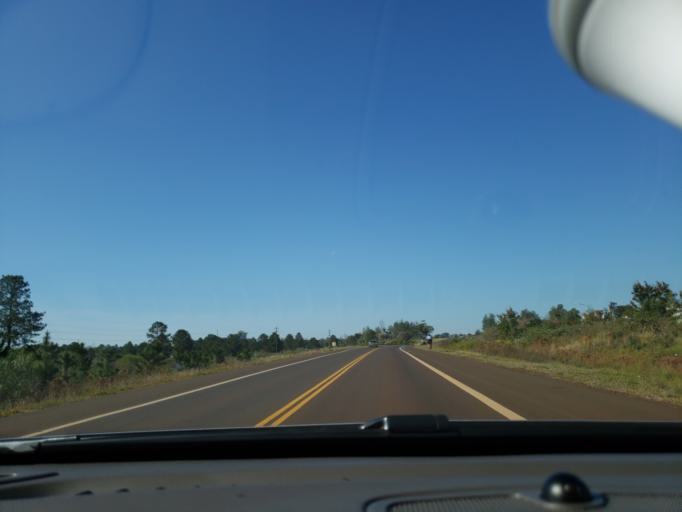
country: AR
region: Misiones
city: Garupa
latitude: -27.4632
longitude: -55.8764
